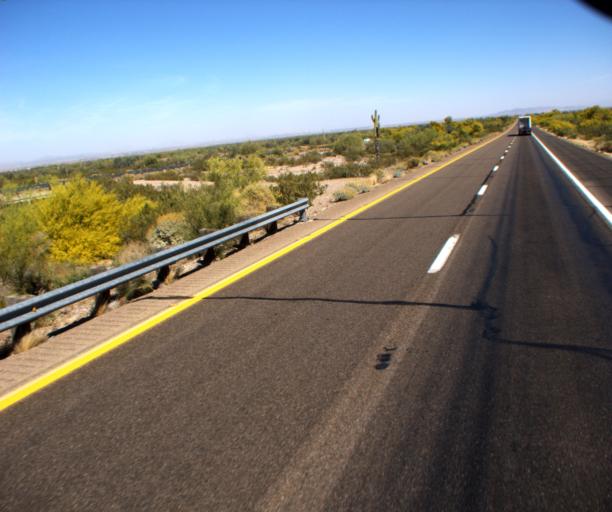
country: US
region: Arizona
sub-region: Pinal County
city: Maricopa
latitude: 32.8308
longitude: -112.0451
